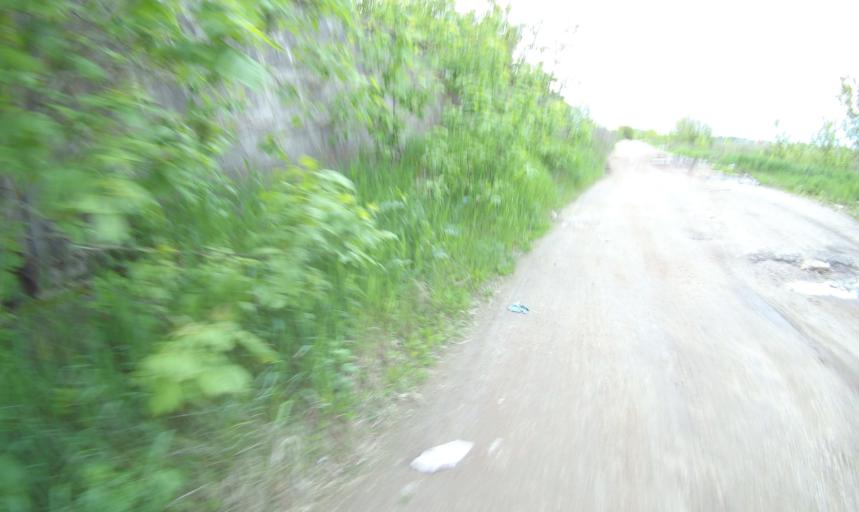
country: RU
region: Moskovskaya
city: Ramenskoye
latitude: 55.5598
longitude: 38.2824
